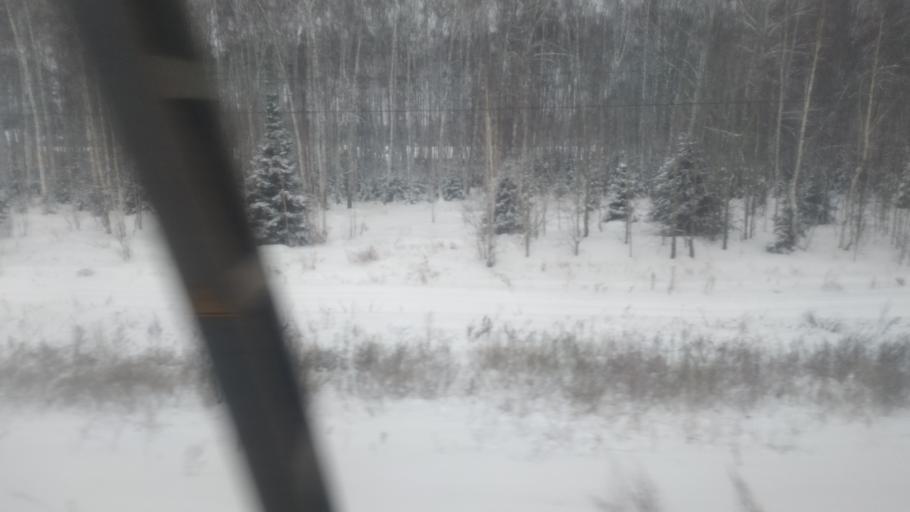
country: RU
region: Udmurtiya
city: Malaya Purga
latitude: 56.5556
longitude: 53.1201
